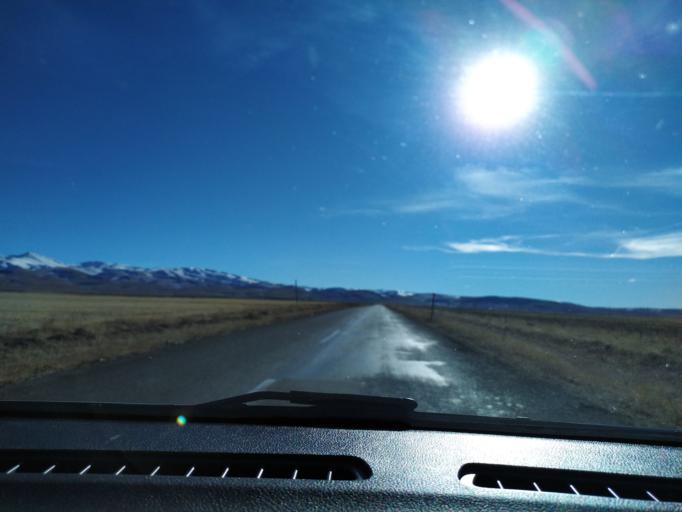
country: TR
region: Kayseri
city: Orensehir
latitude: 38.8876
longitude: 36.7287
